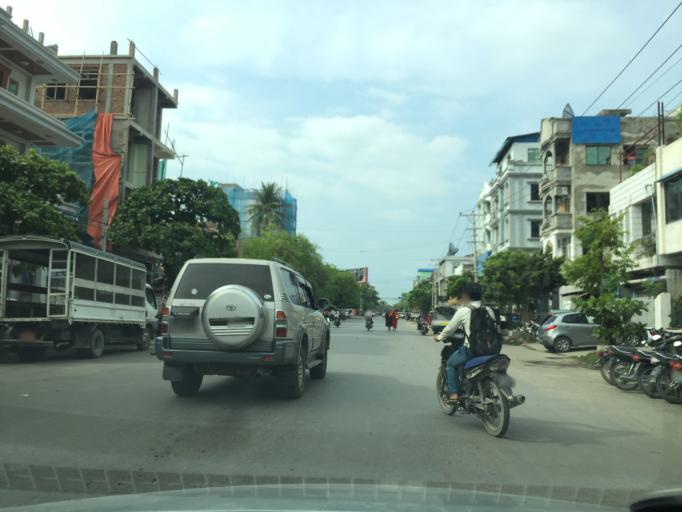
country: MM
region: Mandalay
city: Mandalay
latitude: 21.9709
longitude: 96.0804
